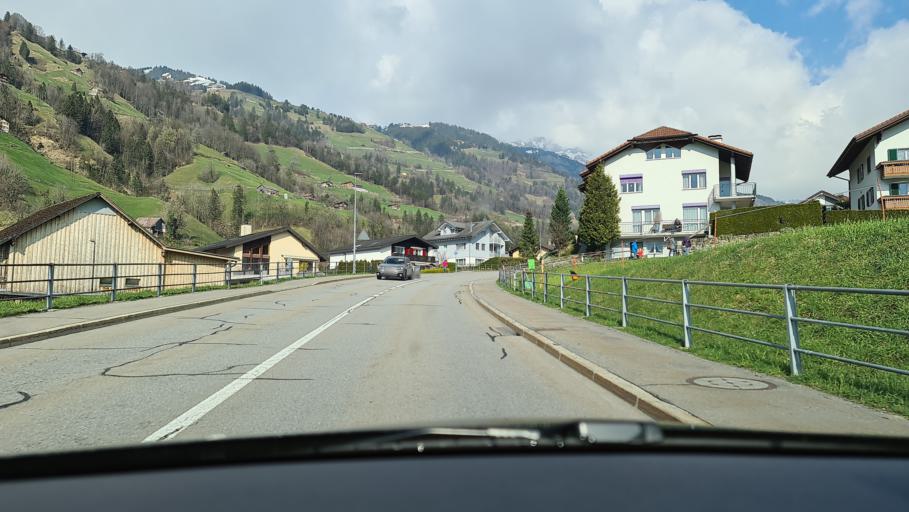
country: CH
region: Uri
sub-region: Uri
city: Burglen
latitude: 46.8766
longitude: 8.6730
